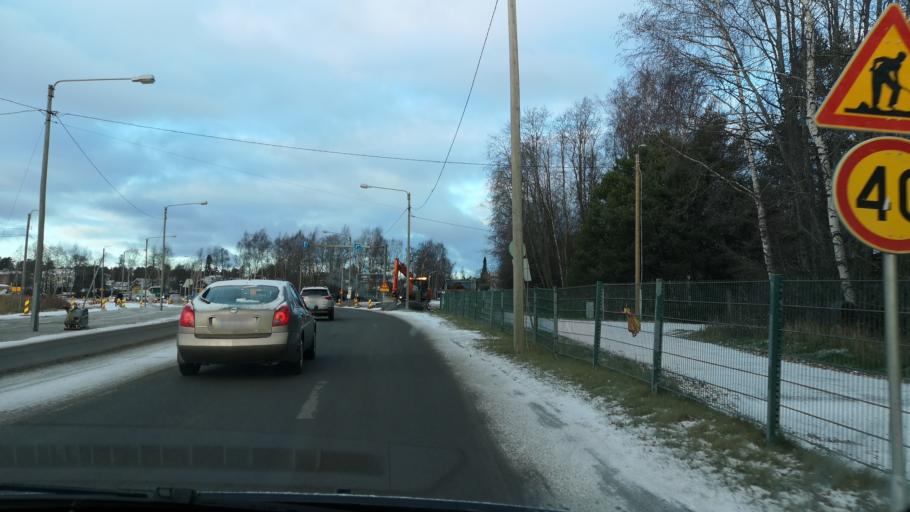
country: FI
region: Ostrobothnia
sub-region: Vaasa
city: Vaasa
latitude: 63.1124
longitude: 21.6187
